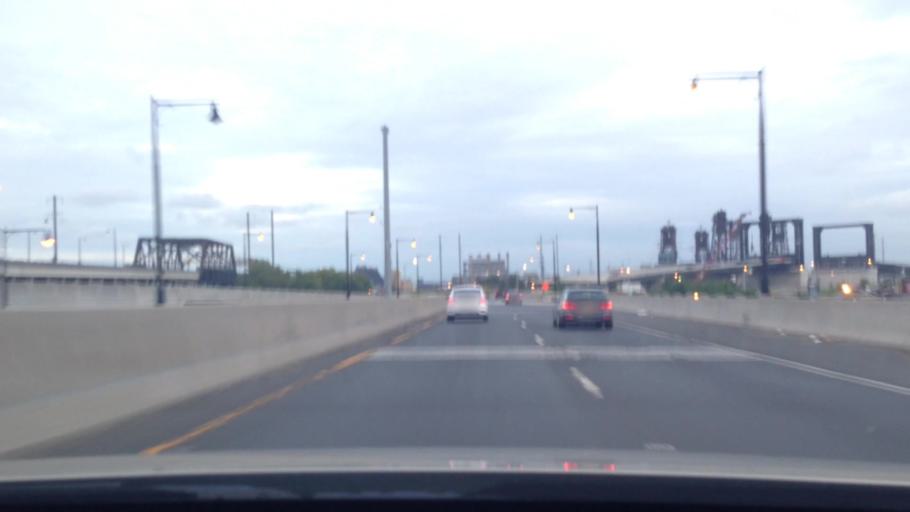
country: US
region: New Jersey
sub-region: Hudson County
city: Jersey City
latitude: 40.7394
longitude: -74.0720
